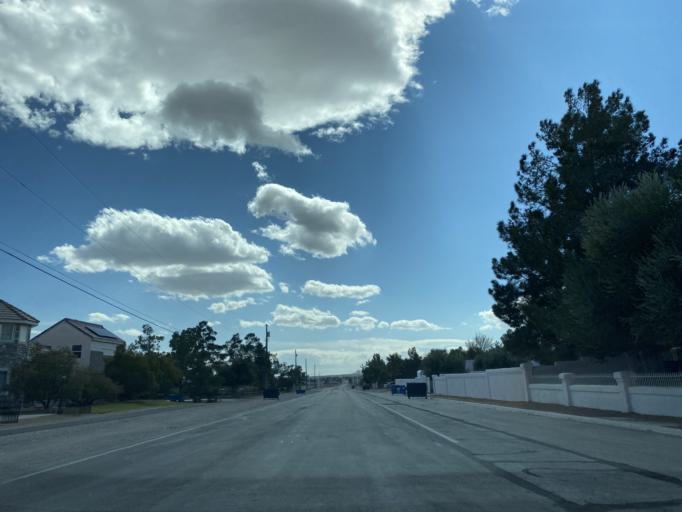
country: US
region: Nevada
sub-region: Clark County
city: Summerlin South
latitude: 36.2521
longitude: -115.2884
